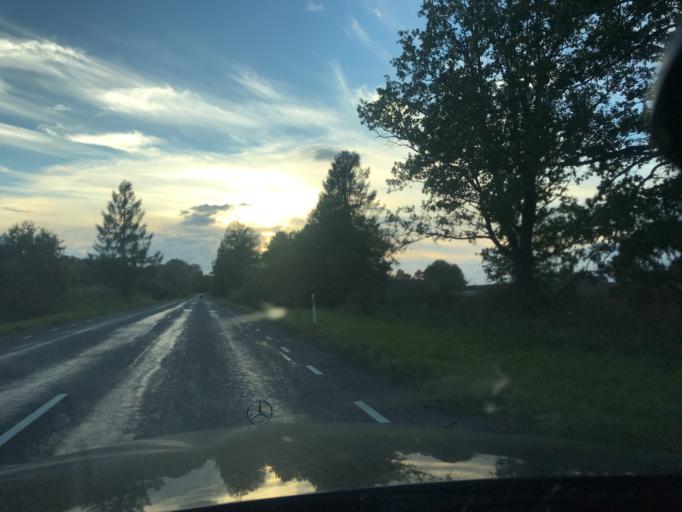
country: EE
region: Vorumaa
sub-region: Antsla vald
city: Vana-Antsla
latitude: 57.8829
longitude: 26.5557
